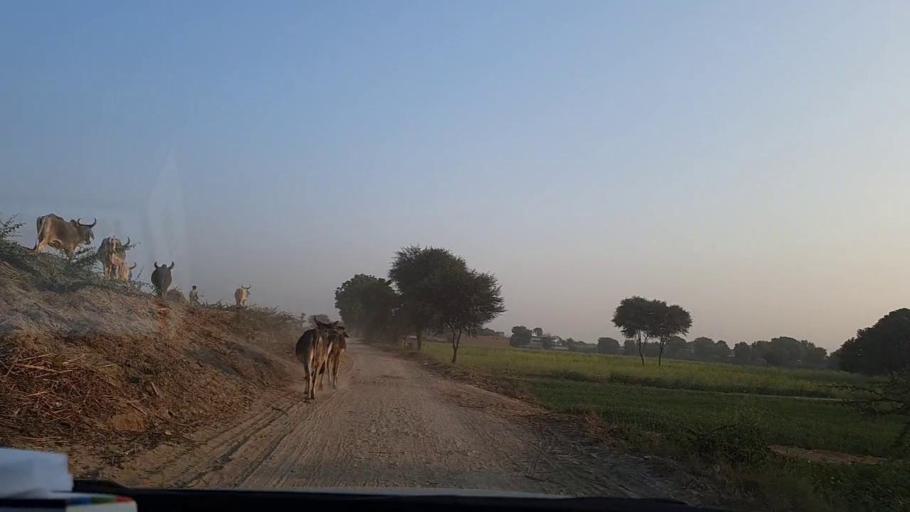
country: PK
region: Sindh
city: Tando Ghulam Ali
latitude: 25.1776
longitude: 68.9253
